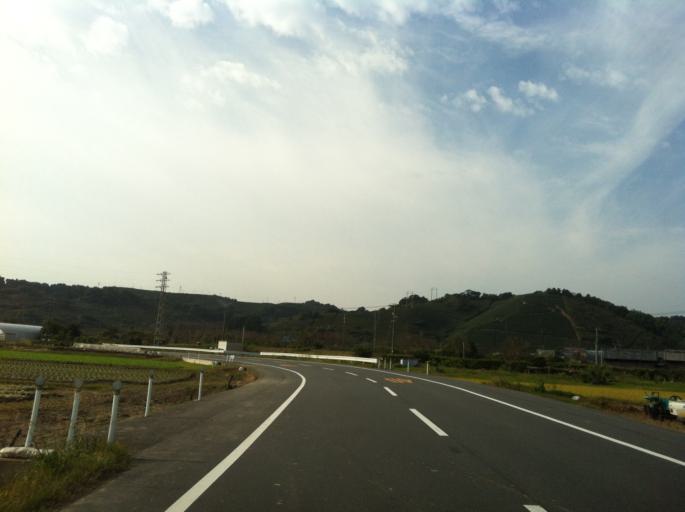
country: JP
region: Shizuoka
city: Sagara
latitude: 34.7513
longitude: 138.2061
